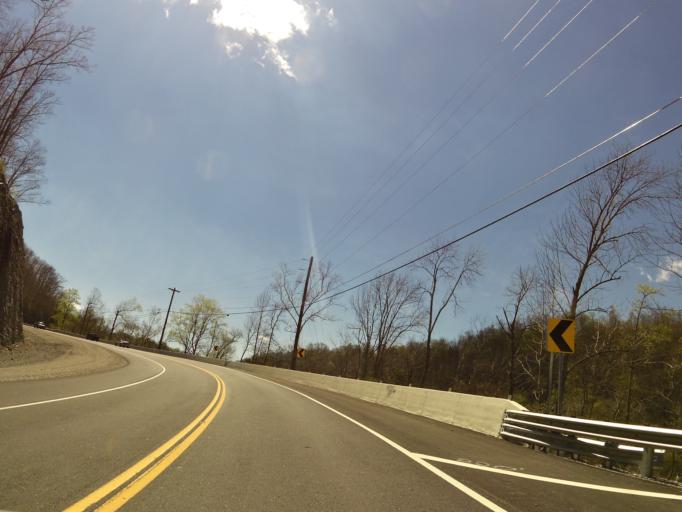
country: US
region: Tennessee
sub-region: DeKalb County
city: Smithville
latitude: 35.9659
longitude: -85.7194
